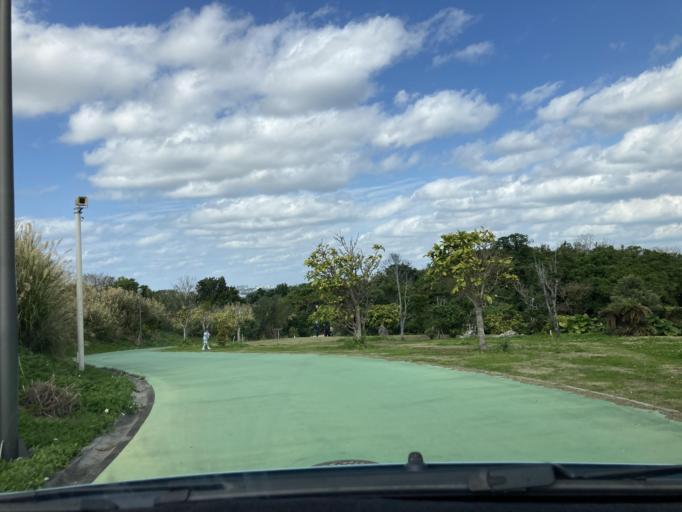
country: JP
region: Okinawa
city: Ginowan
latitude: 26.1865
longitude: 127.7622
